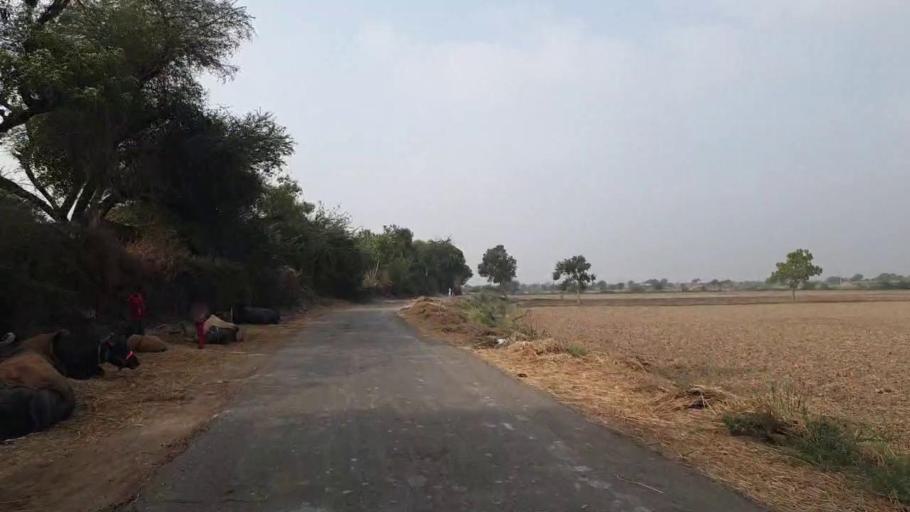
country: PK
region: Sindh
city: Matli
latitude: 24.9882
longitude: 68.6331
